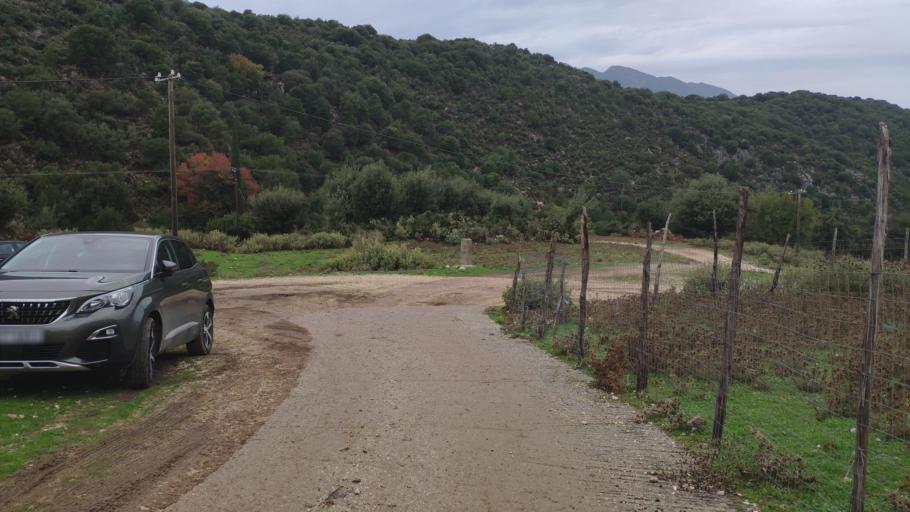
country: GR
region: Epirus
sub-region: Nomos Prevezis
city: Kanalaki
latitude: 39.3624
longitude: 20.6415
